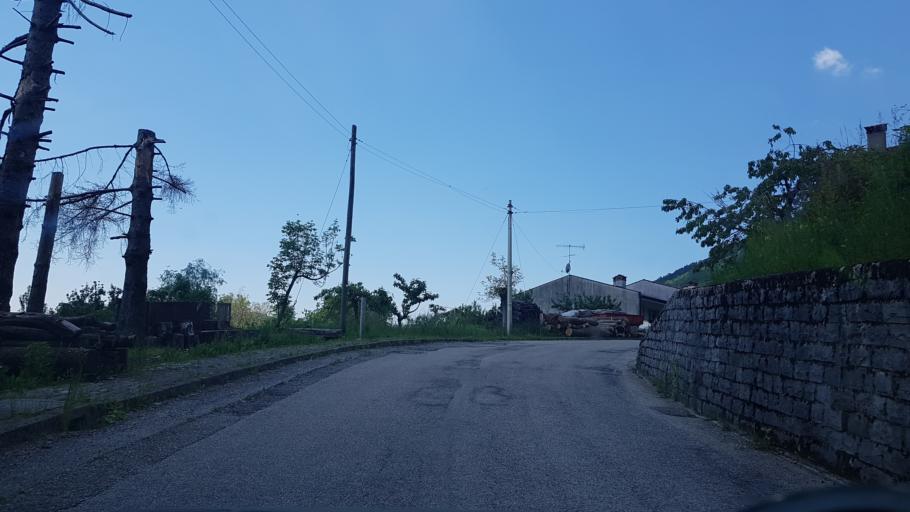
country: IT
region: Friuli Venezia Giulia
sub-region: Provincia di Udine
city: Torreano
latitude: 46.1722
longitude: 13.4330
